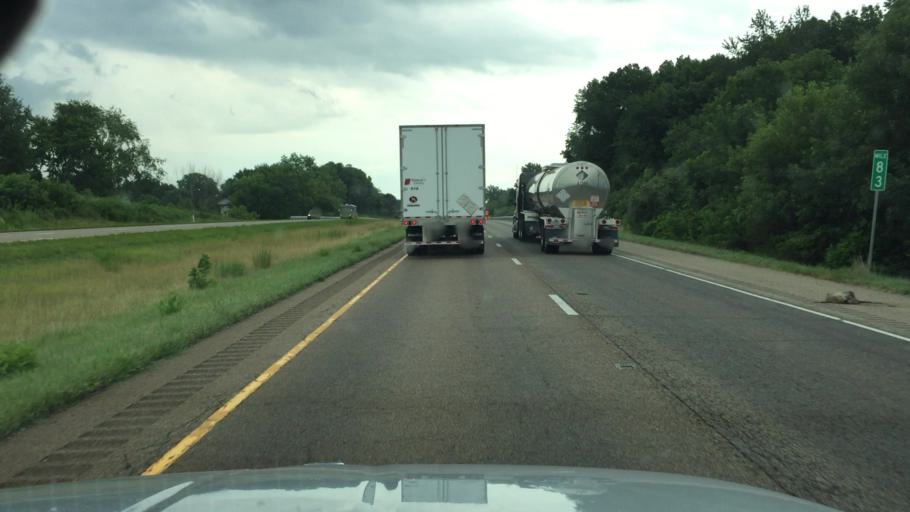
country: US
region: Illinois
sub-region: Peoria County
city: Hanna City
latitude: 40.7664
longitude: -89.7339
